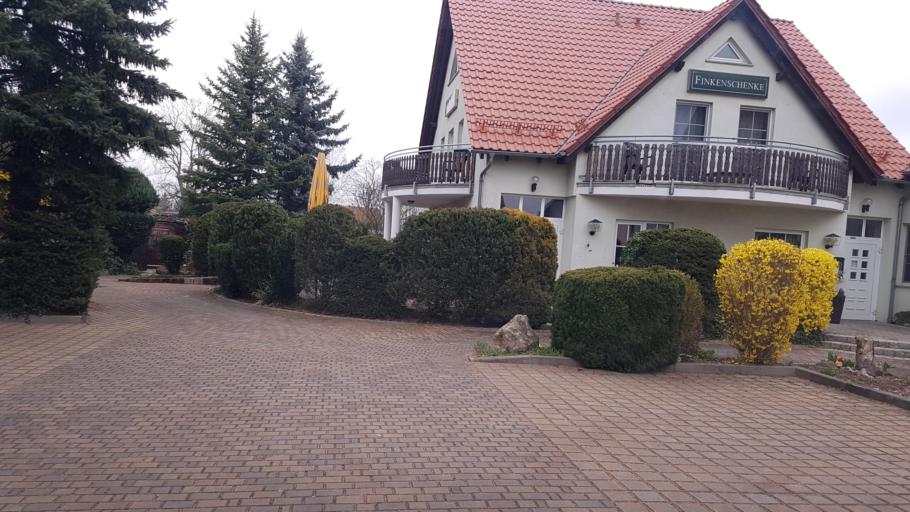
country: DE
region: Saxony
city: Nauwalde
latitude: 51.4214
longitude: 13.4483
